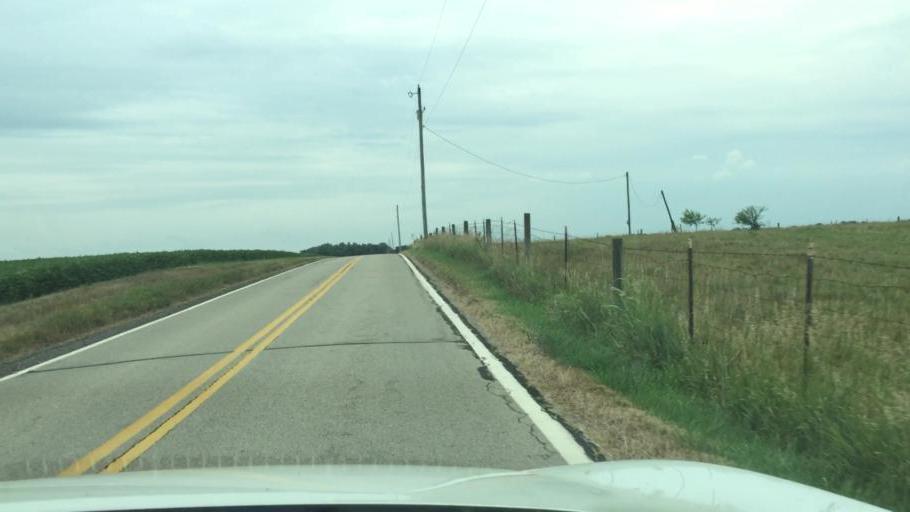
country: US
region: Ohio
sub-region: Clark County
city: Northridge
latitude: 39.9971
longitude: -83.6943
